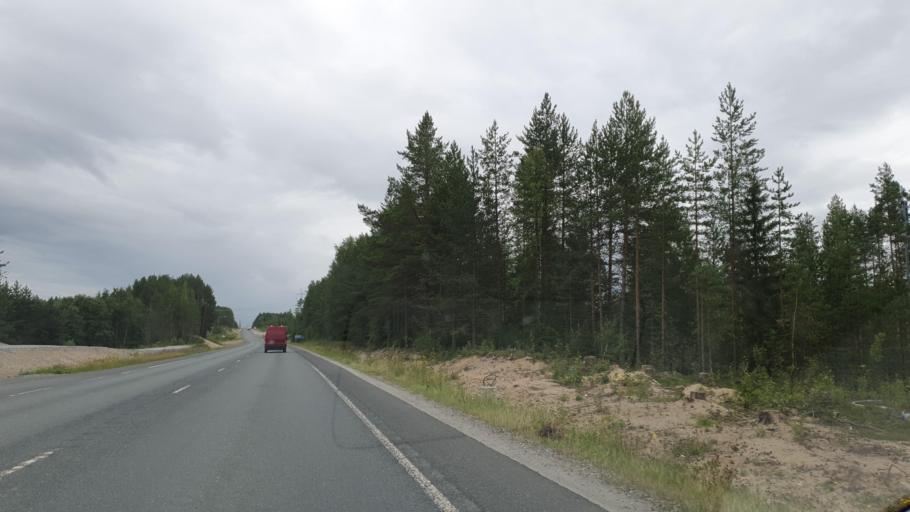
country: FI
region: Northern Savo
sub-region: Ylae-Savo
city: Lapinlahti
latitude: 63.2772
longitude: 27.4580
